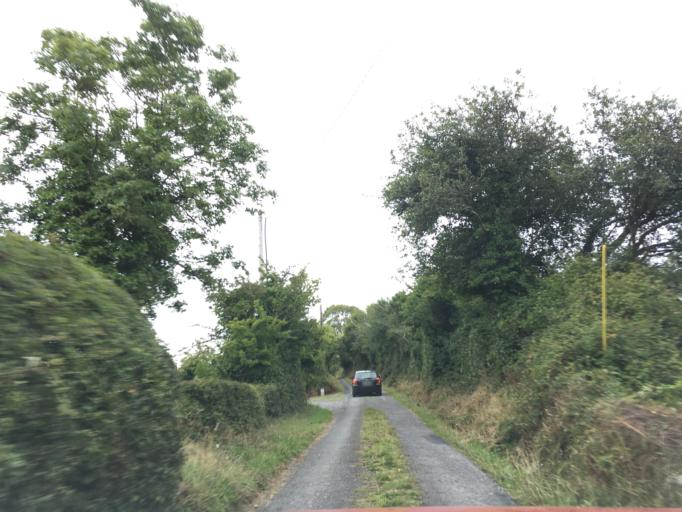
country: IE
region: Munster
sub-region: County Limerick
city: Askeaton
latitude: 52.7167
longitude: -9.0621
